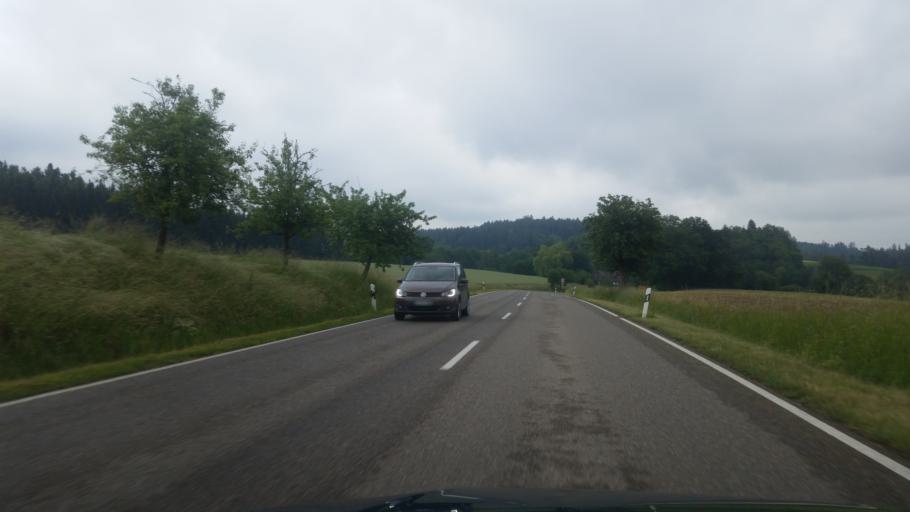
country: DE
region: Baden-Wuerttemberg
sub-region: Regierungsbezirk Stuttgart
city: Rosenberg
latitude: 49.0257
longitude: 9.9862
